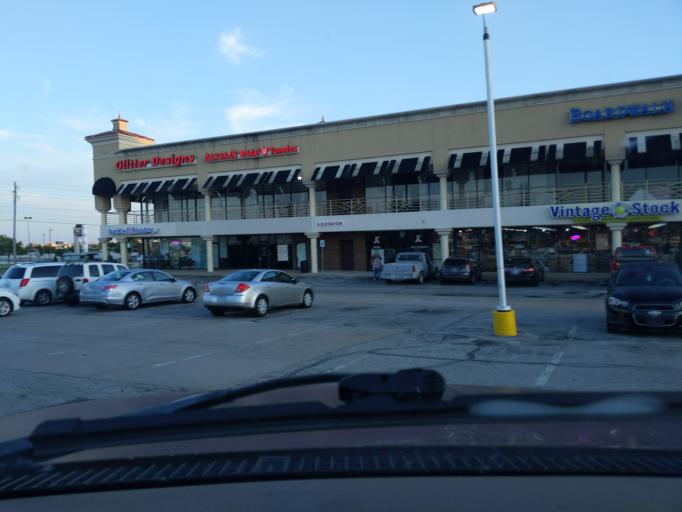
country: US
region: Oklahoma
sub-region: Tulsa County
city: Jenks
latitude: 36.0641
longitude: -95.8874
